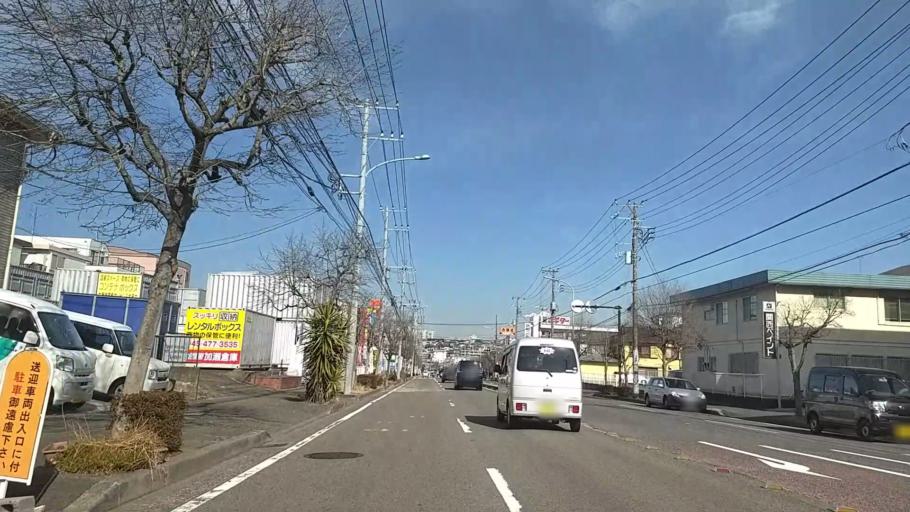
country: JP
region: Kanagawa
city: Kamakura
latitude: 35.3774
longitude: 139.5806
